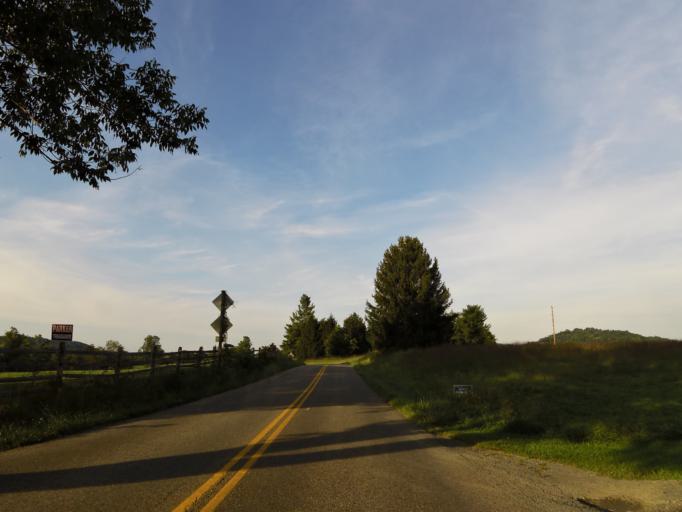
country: US
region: Virginia
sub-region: Washington County
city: Abingdon
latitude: 36.6787
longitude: -81.9329
